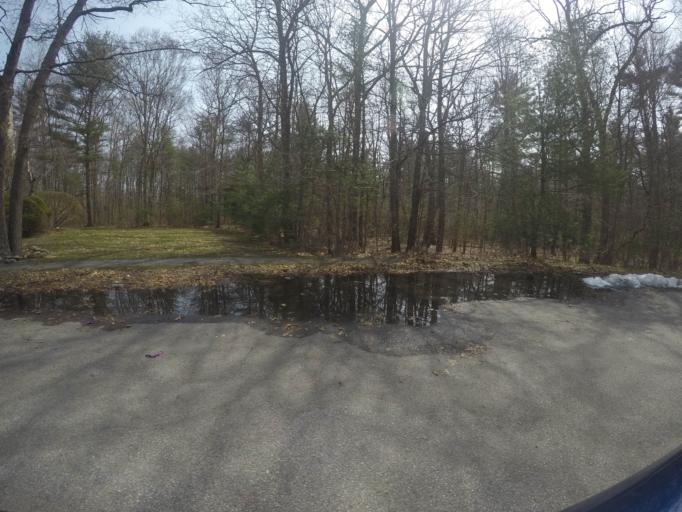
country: US
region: Massachusetts
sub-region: Bristol County
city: Easton
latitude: 42.0399
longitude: -71.1068
